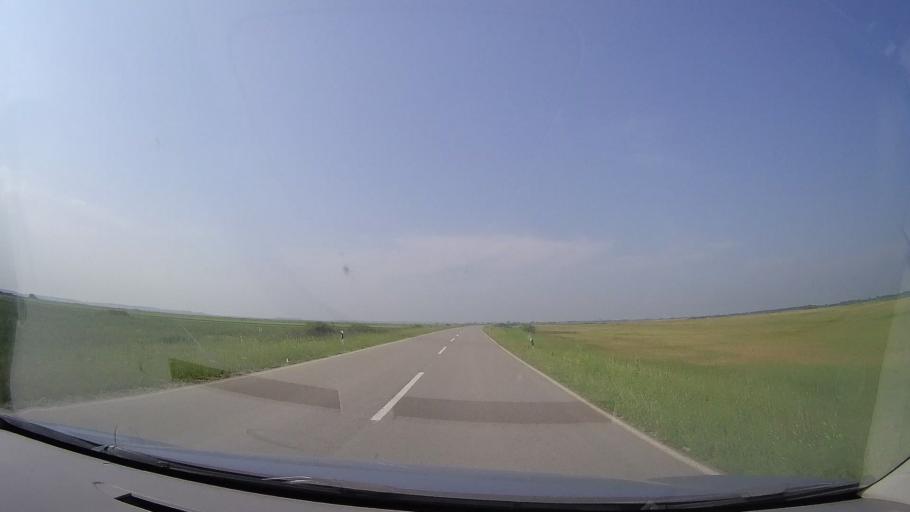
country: RS
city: Jasa Tomic
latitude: 45.4164
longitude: 20.8325
